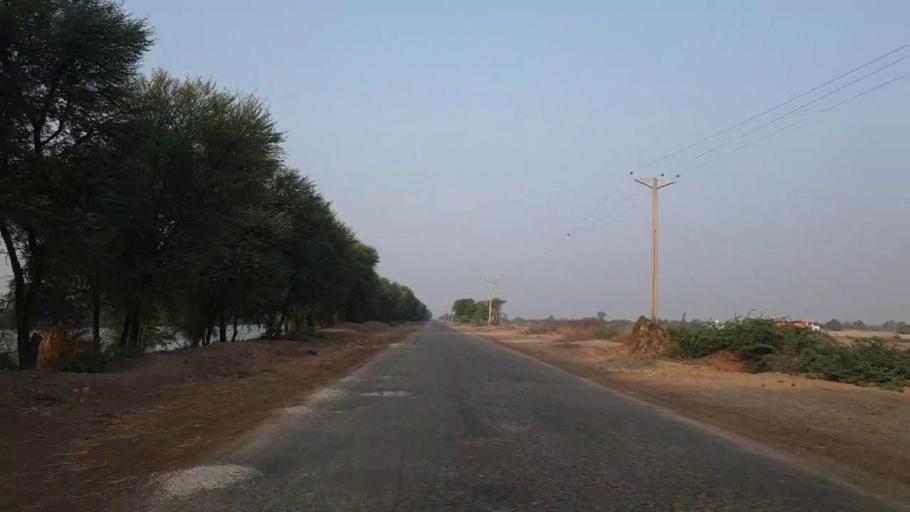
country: PK
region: Sindh
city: Tando Muhammad Khan
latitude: 25.1217
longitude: 68.4294
